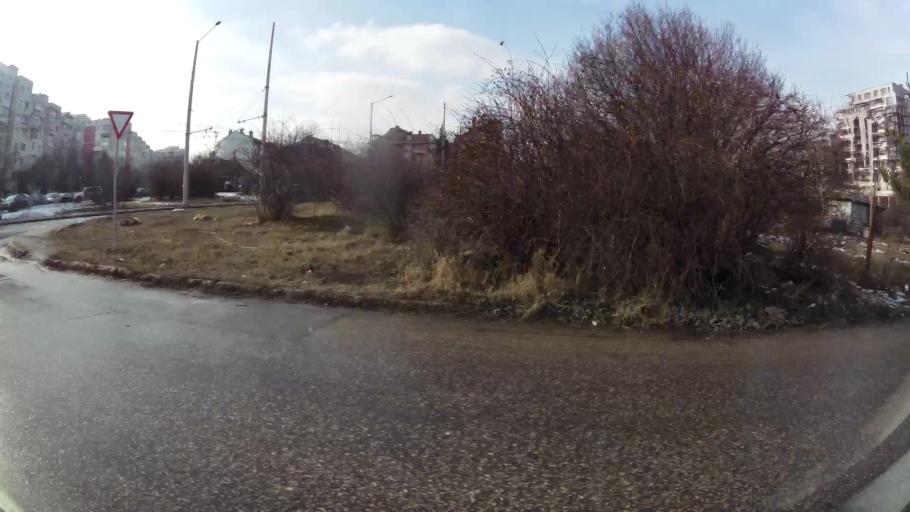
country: BG
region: Sofiya
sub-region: Obshtina Bozhurishte
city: Bozhurishte
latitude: 42.7233
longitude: 23.2606
